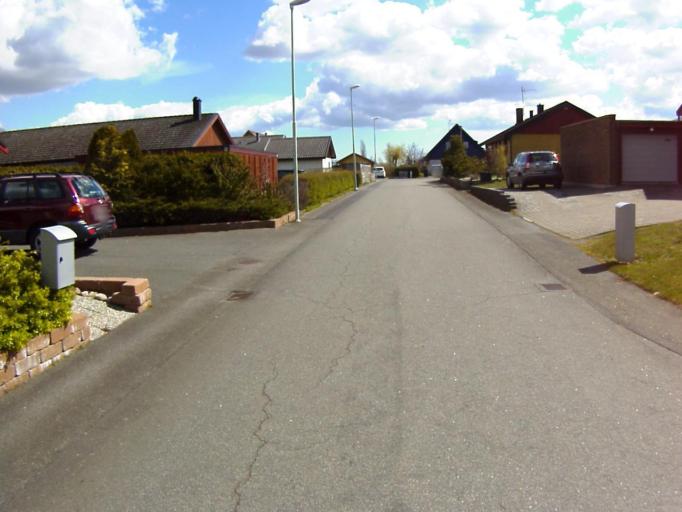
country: SE
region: Skane
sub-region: Kristianstads Kommun
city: Kristianstad
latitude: 56.0145
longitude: 14.0998
